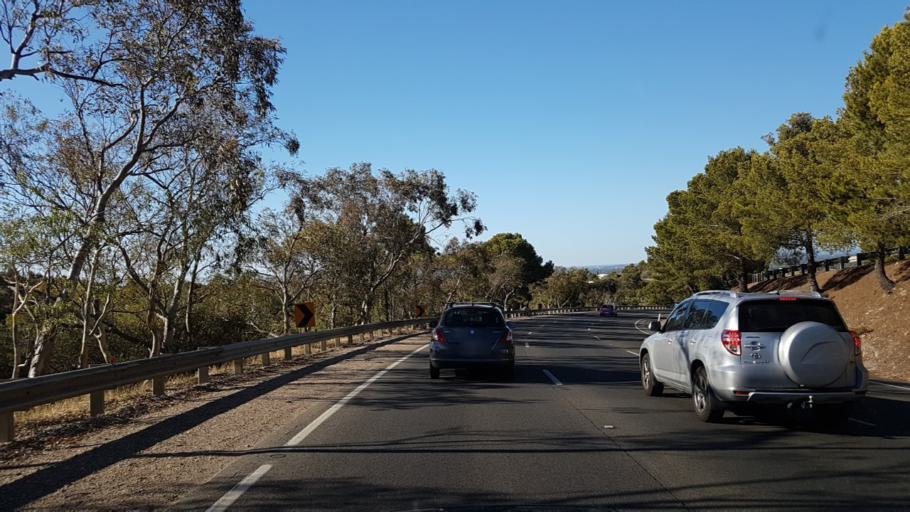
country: AU
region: South Australia
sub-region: Onkaparinga
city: Bedford Park
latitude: -35.0399
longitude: 138.5592
